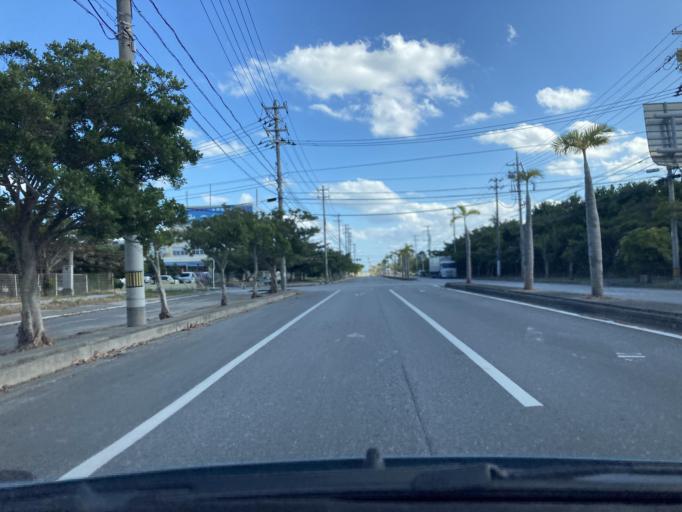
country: JP
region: Okinawa
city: Katsuren-haebaru
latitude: 26.3335
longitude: 127.8517
